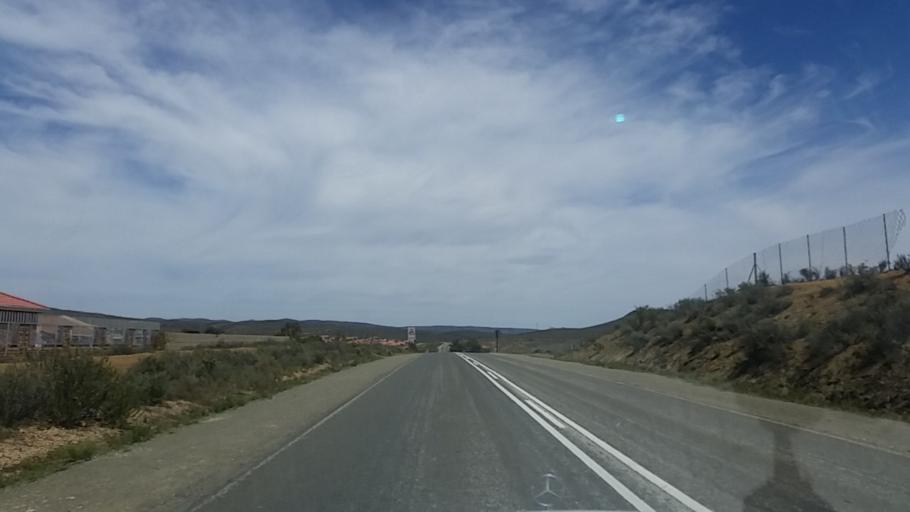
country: ZA
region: Western Cape
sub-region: Eden District Municipality
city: Knysna
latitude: -33.6593
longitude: 23.1137
